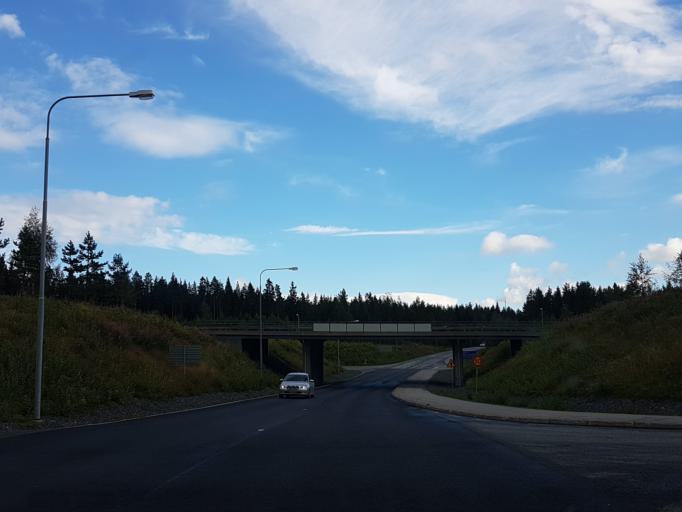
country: SE
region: Vaesterbotten
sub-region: Umea Kommun
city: Saevar
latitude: 63.8997
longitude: 20.5632
